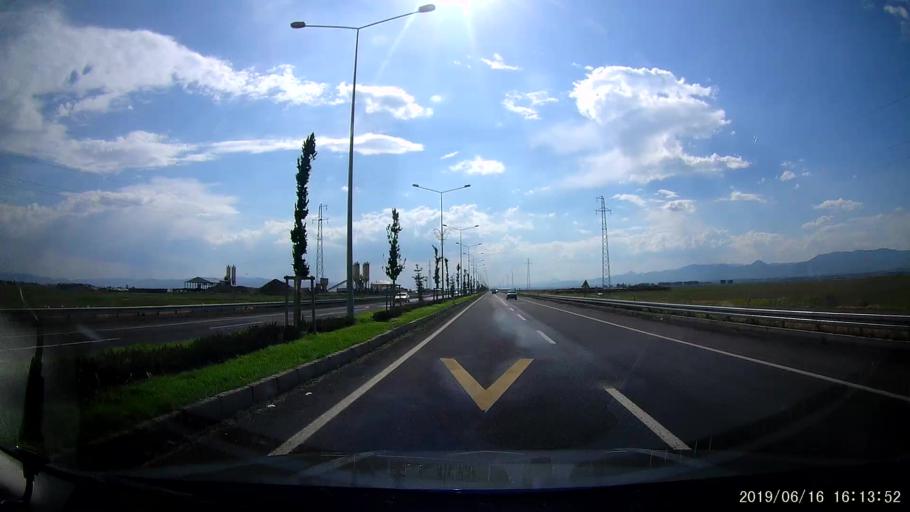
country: TR
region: Erzurum
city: Erzurum
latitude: 39.9600
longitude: 41.2629
